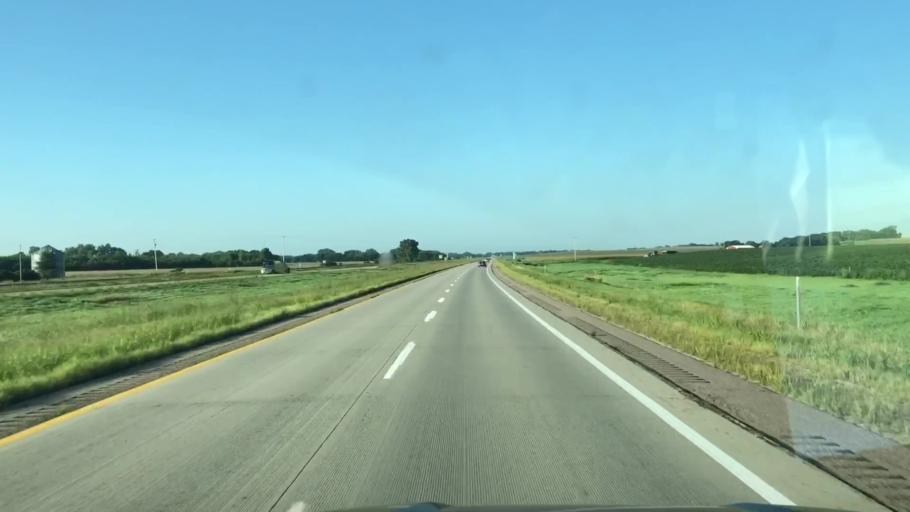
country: US
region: Iowa
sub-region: Plymouth County
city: Le Mars
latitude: 42.8828
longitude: -96.0992
